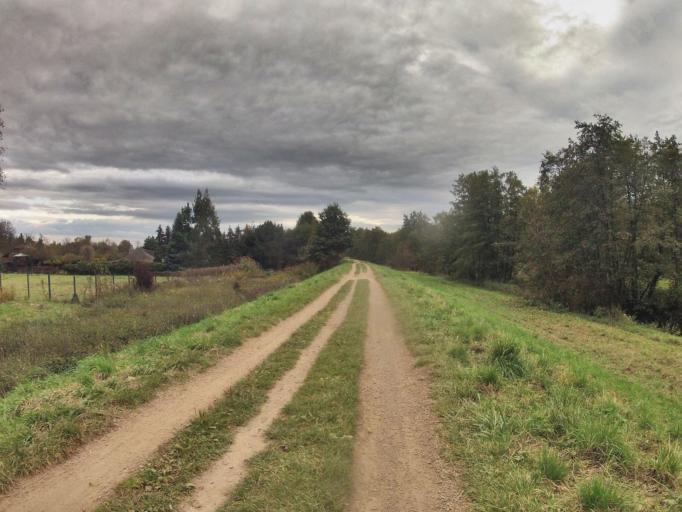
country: PL
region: Lesser Poland Voivodeship
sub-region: Krakow
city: Krakow
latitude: 50.0647
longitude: 19.8928
